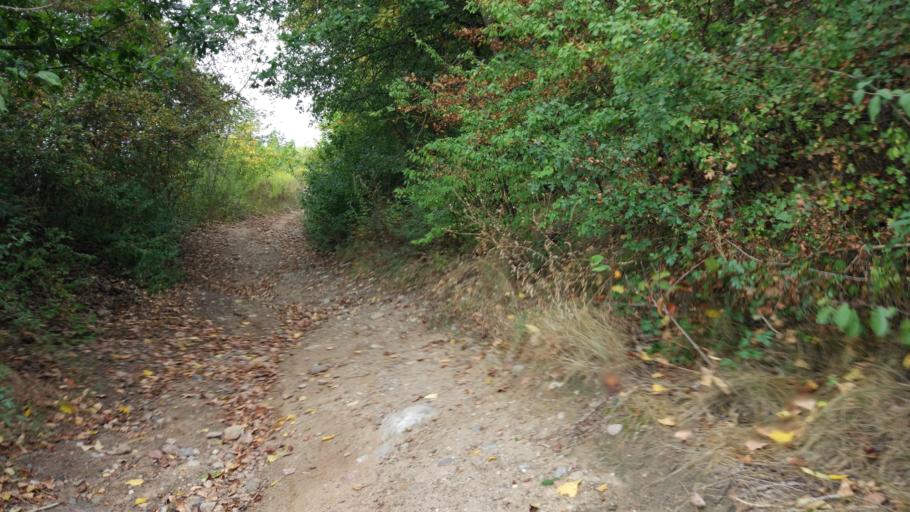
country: PL
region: Masovian Voivodeship
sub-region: Plock
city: Plock
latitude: 52.5268
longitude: 19.7474
